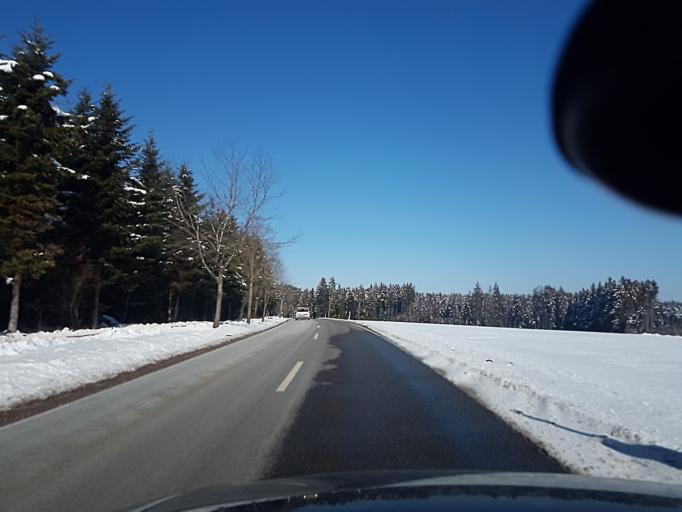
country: DE
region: Baden-Wuerttemberg
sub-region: Freiburg Region
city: Konigsfeld im Schwarzwald
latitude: 48.1562
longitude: 8.4526
